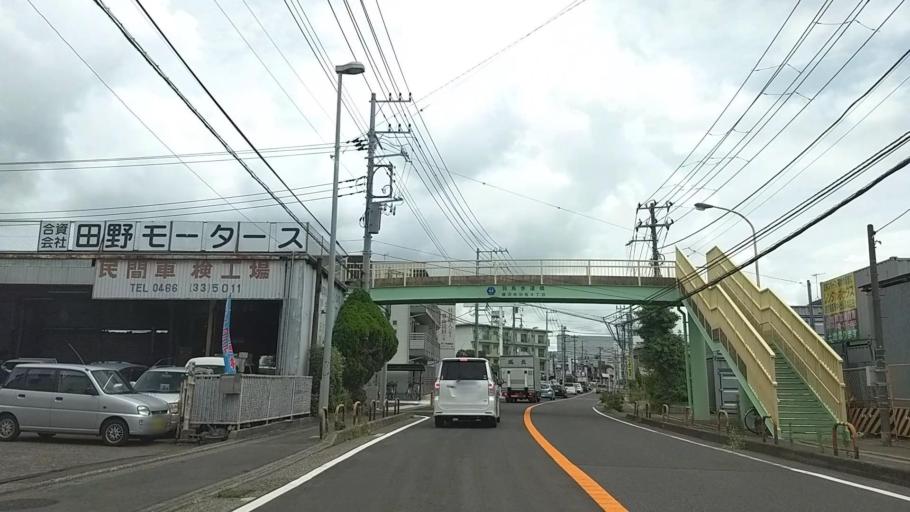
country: JP
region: Kanagawa
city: Fujisawa
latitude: 35.3477
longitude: 139.4586
